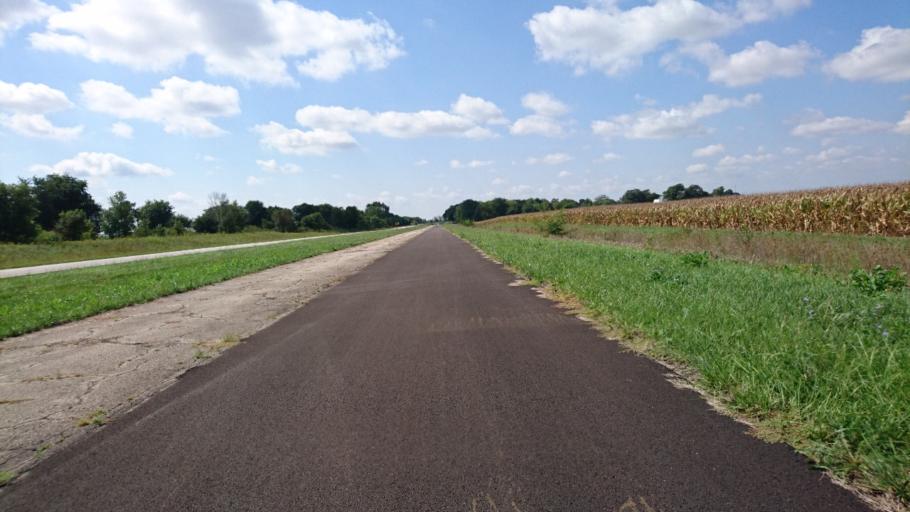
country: US
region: Illinois
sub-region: McLean County
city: Lexington
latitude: 40.5855
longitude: -88.8667
